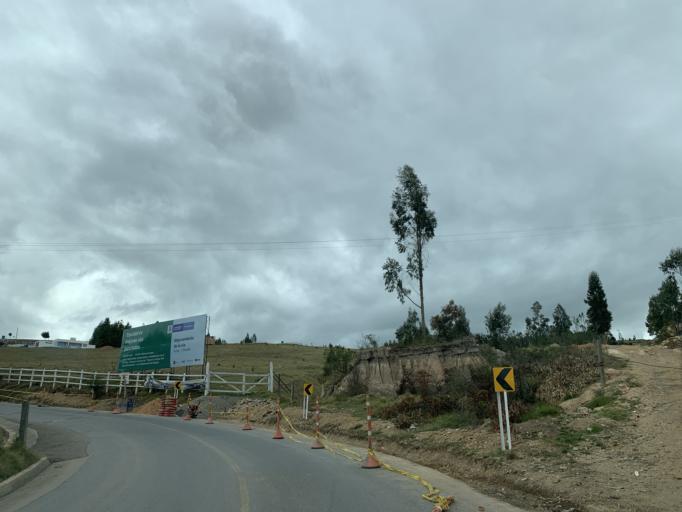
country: CO
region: Boyaca
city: Tunja
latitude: 5.5307
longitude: -73.3381
